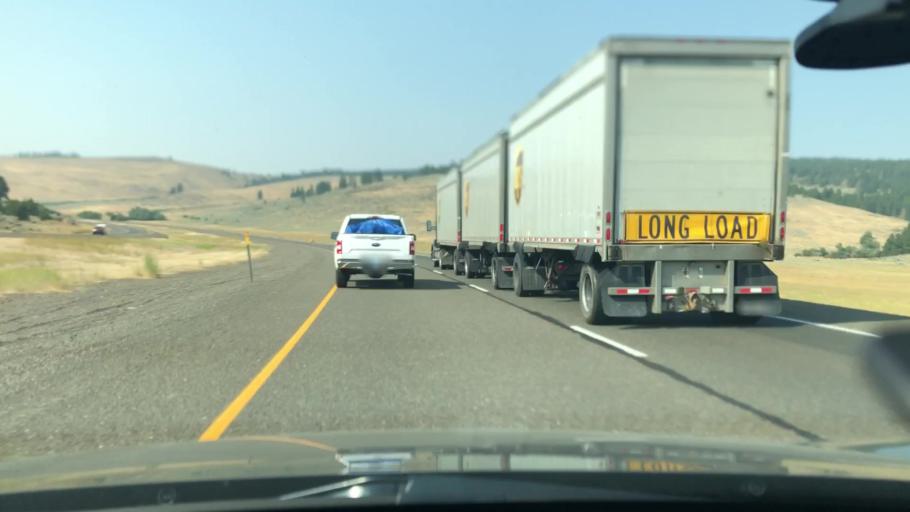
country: US
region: Oregon
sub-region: Union County
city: Union
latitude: 45.1599
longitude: -117.9644
